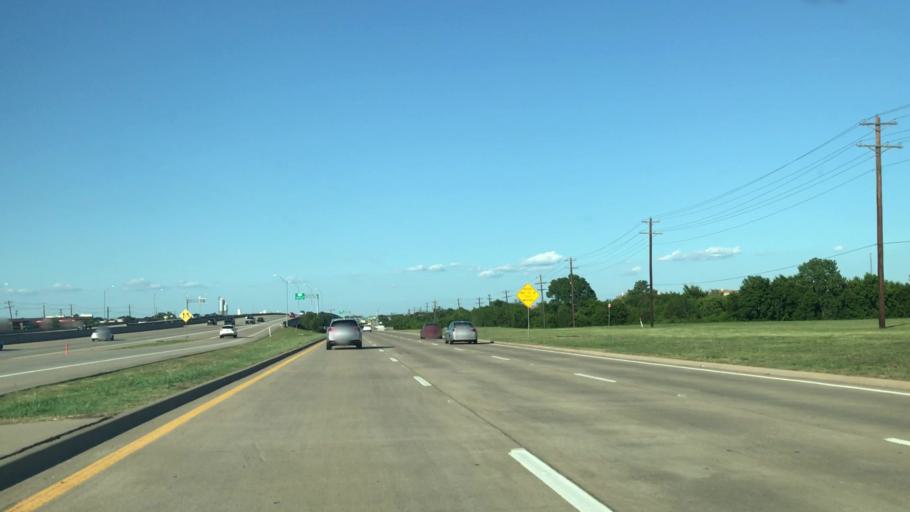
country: US
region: Texas
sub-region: Collin County
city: Frisco
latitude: 33.1168
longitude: -96.7554
